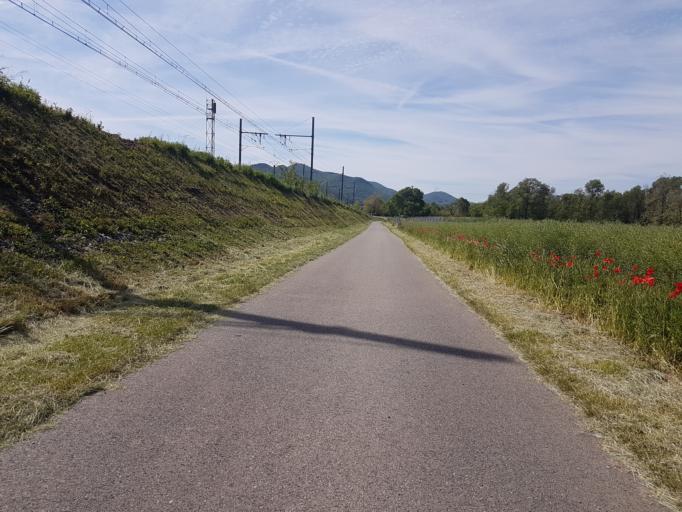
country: FR
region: Rhone-Alpes
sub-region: Departement de l'Ardeche
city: Le Pouzin
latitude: 44.7341
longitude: 4.7470
